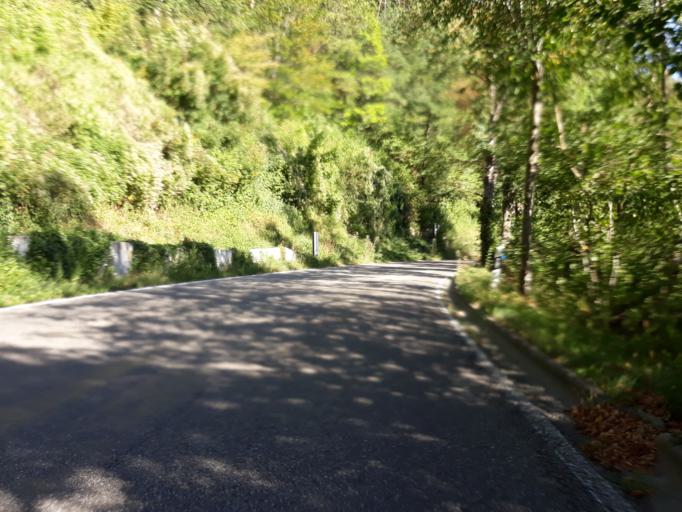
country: DE
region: Baden-Wuerttemberg
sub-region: Regierungsbezirk Stuttgart
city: Ehningen
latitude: 48.6639
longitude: 8.9196
